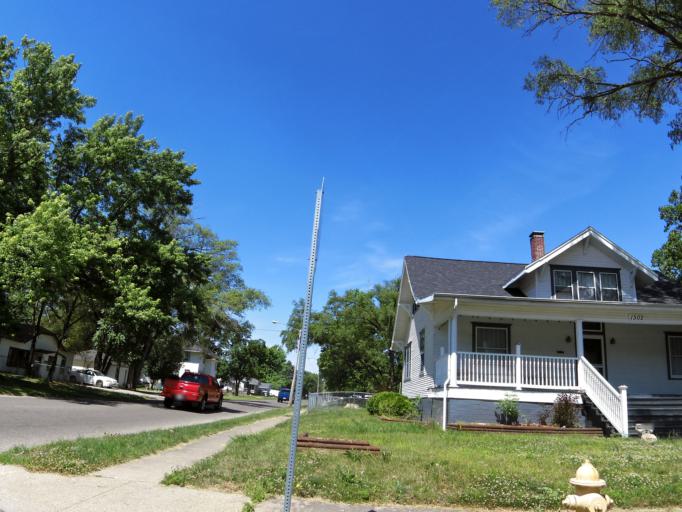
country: US
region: Illinois
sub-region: Vermilion County
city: Danville
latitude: 40.1458
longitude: -87.6330
